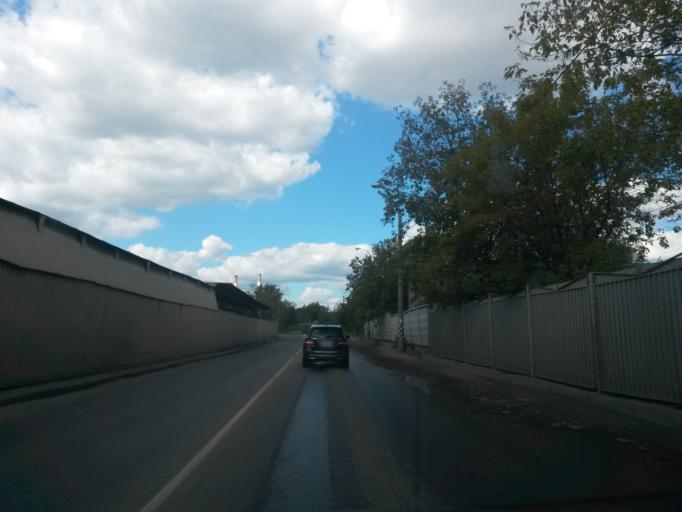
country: RU
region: Moskovskaya
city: Kozhukhovo
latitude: 55.7073
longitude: 37.7024
